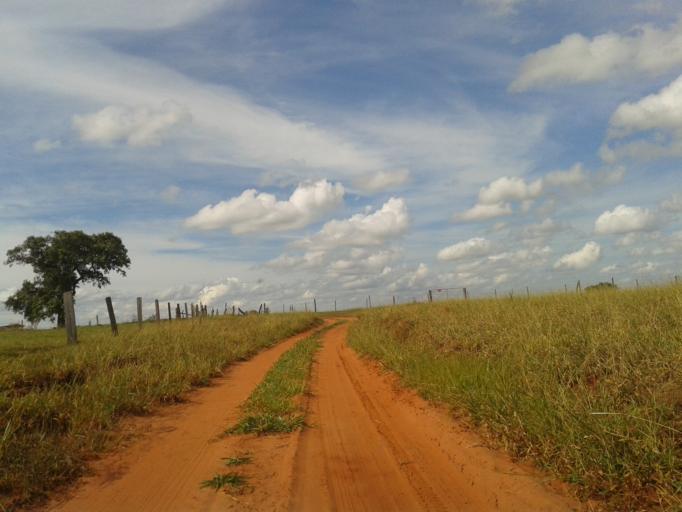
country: BR
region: Minas Gerais
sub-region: Campina Verde
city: Campina Verde
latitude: -19.4524
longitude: -49.6699
